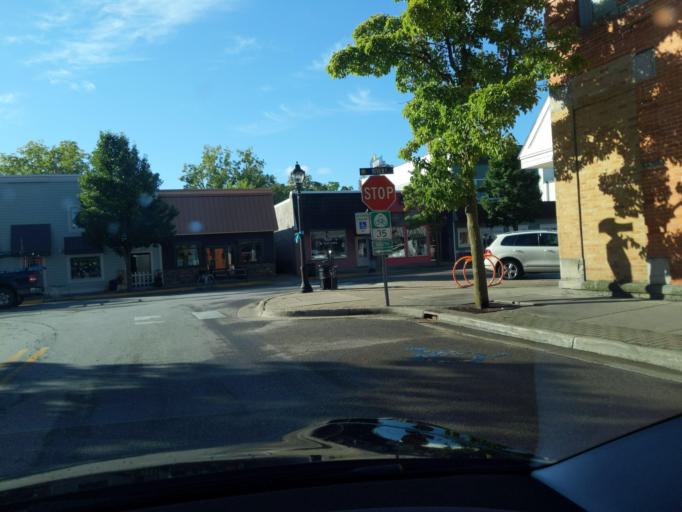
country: US
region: Michigan
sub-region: Antrim County
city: Elk Rapids
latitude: 44.8986
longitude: -85.4127
